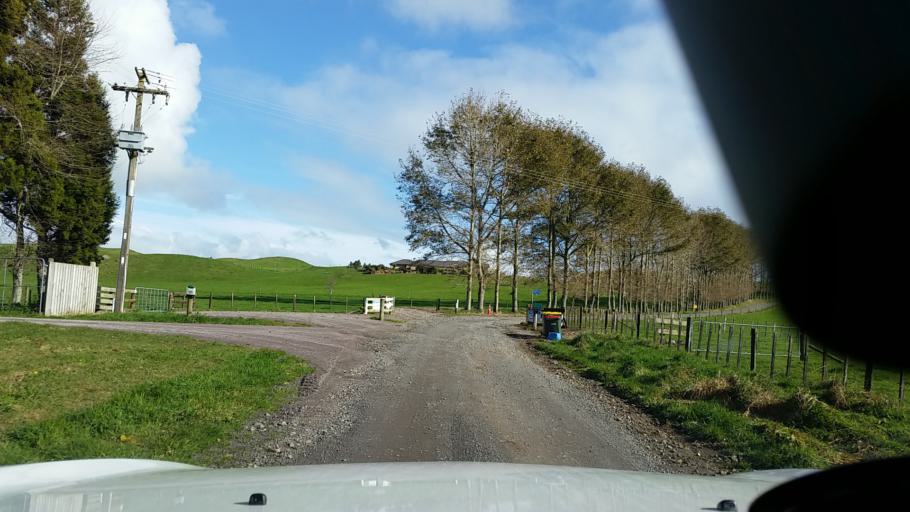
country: NZ
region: Bay of Plenty
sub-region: Rotorua District
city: Rotorua
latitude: -38.0093
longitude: 176.1949
